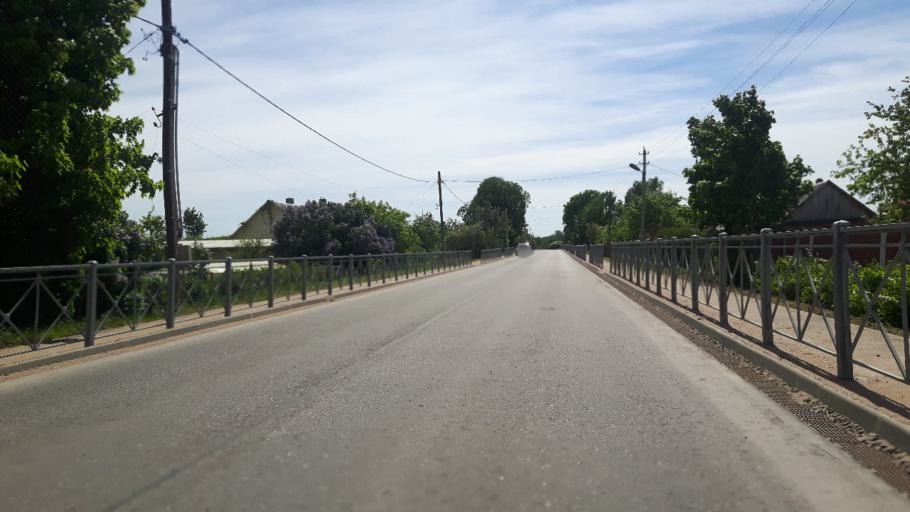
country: RU
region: Leningrad
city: Ust'-Luga
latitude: 59.5900
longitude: 28.1954
